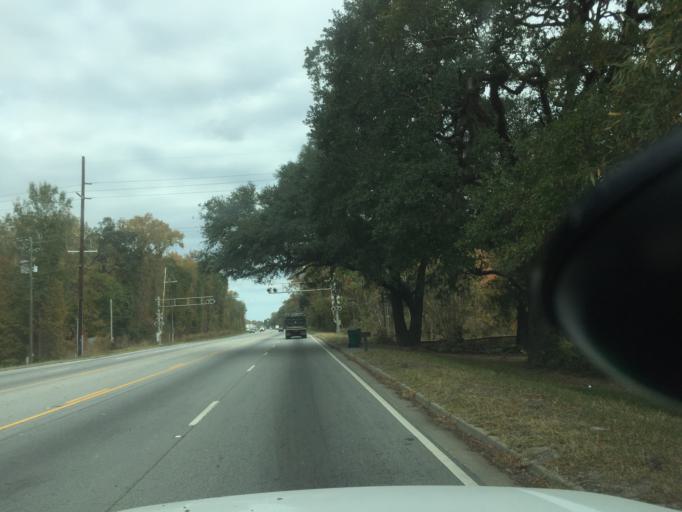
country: US
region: Georgia
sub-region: Chatham County
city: Garden City
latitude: 32.1006
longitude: -81.1959
